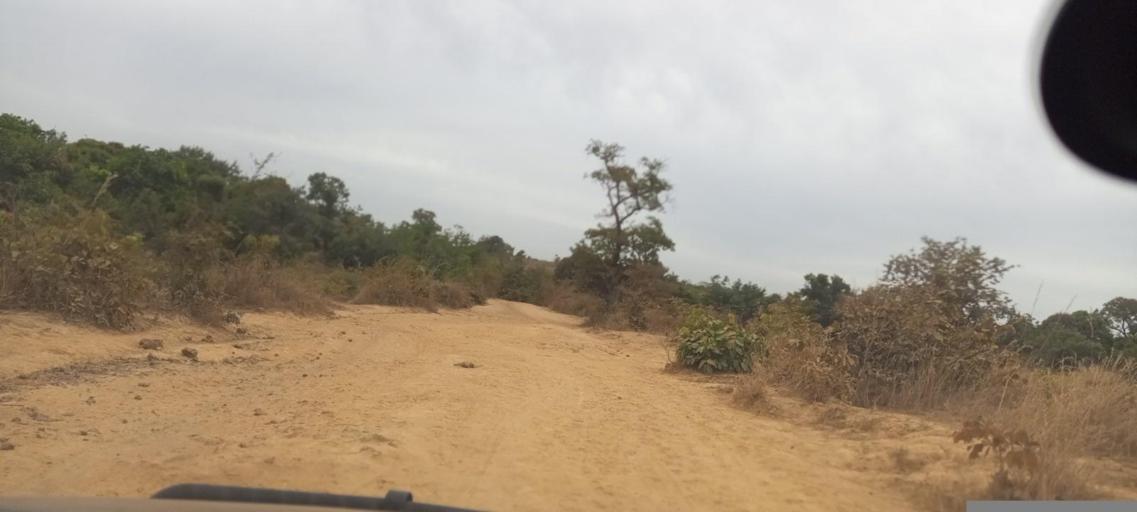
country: ML
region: Koulikoro
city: Kati
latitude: 12.7916
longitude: -8.2552
